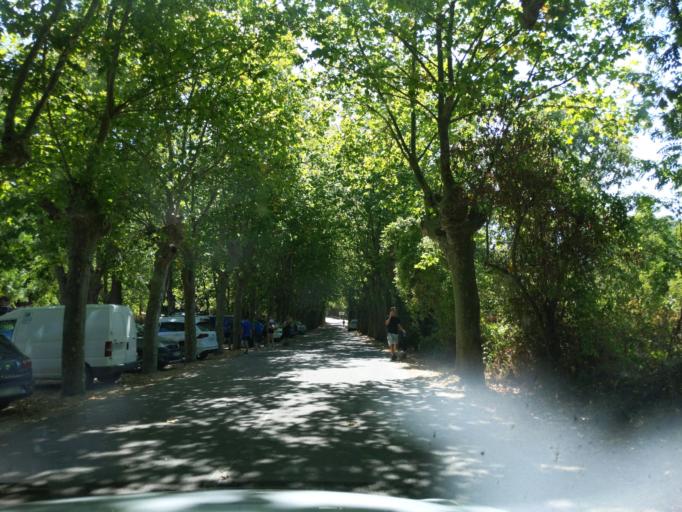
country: ES
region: La Rioja
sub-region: Provincia de La Rioja
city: Ezcaray
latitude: 42.3263
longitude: -3.0101
